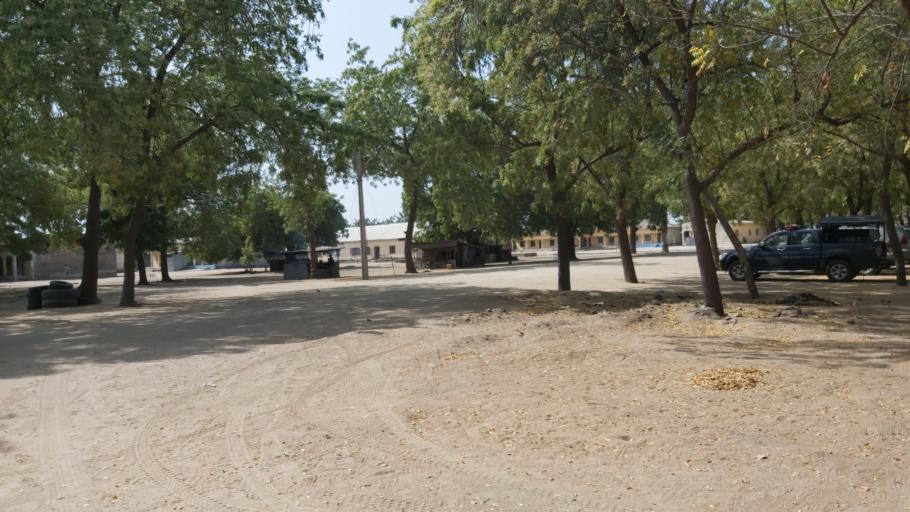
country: CM
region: Far North
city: Mora
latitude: 11.2606
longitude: 14.1551
